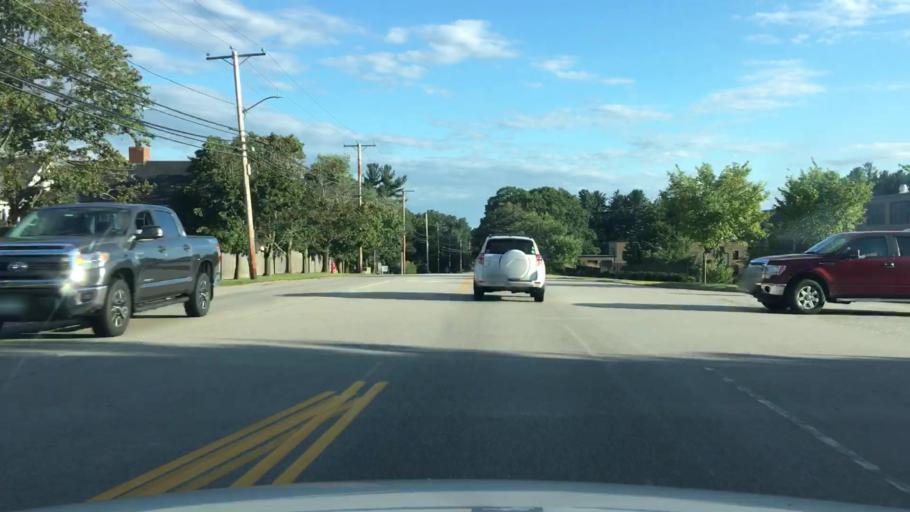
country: US
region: Maine
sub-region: York County
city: Eliot
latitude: 43.1522
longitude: -70.8402
